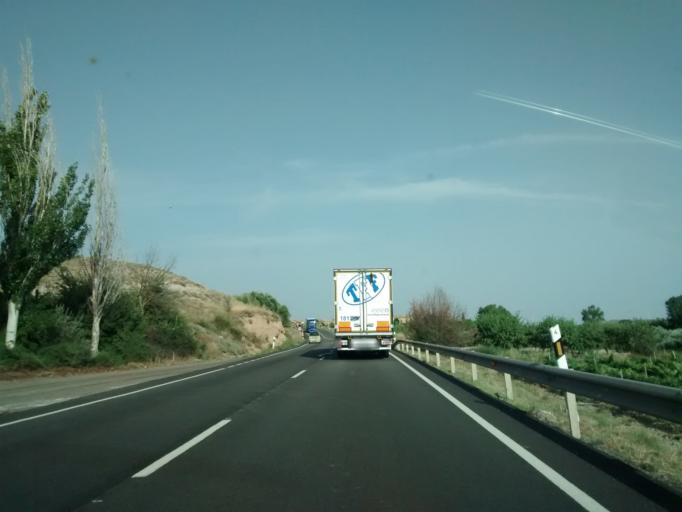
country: ES
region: Aragon
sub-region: Provincia de Zaragoza
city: Malejan
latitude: 41.8291
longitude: -1.5561
